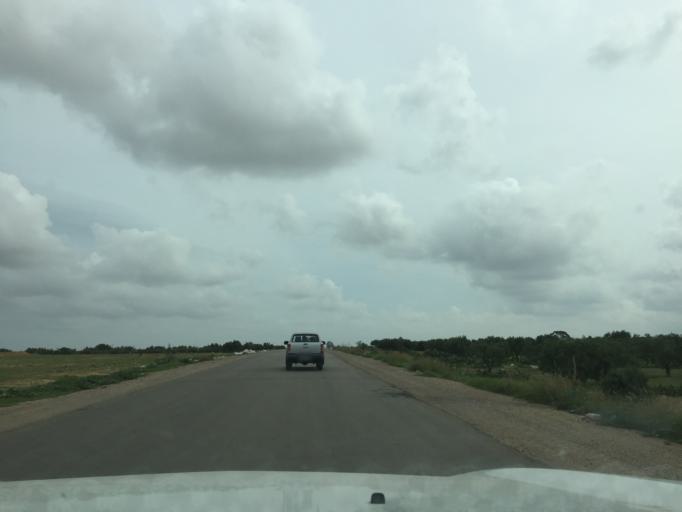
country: TN
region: Al Munastir
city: Jammal
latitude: 35.6069
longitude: 10.7692
